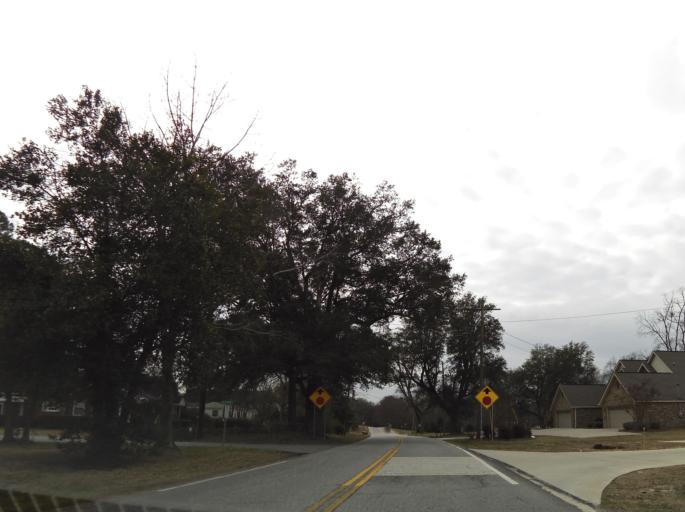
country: US
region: Georgia
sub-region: Peach County
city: Byron
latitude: 32.6530
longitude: -83.7621
